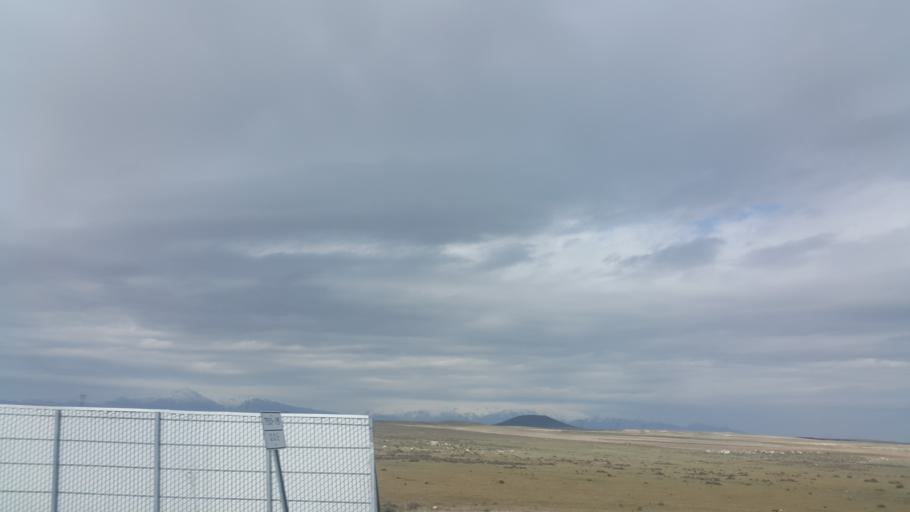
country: TR
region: Nigde
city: Altunhisar
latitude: 37.8885
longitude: 34.1420
